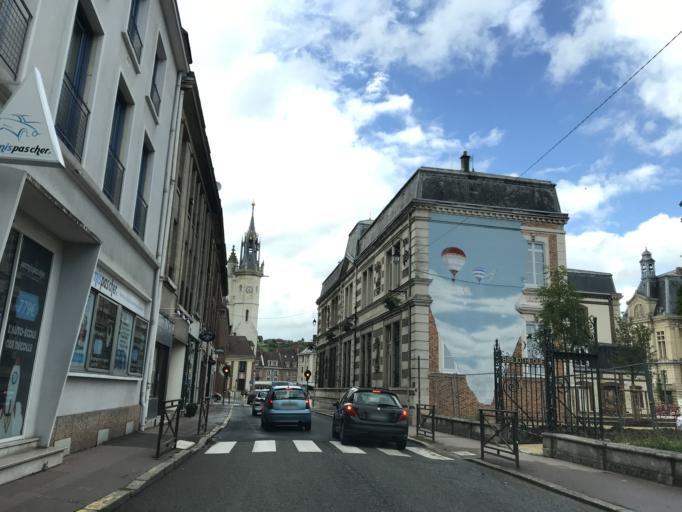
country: FR
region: Haute-Normandie
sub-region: Departement de l'Eure
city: Evreux
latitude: 49.0258
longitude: 1.1508
